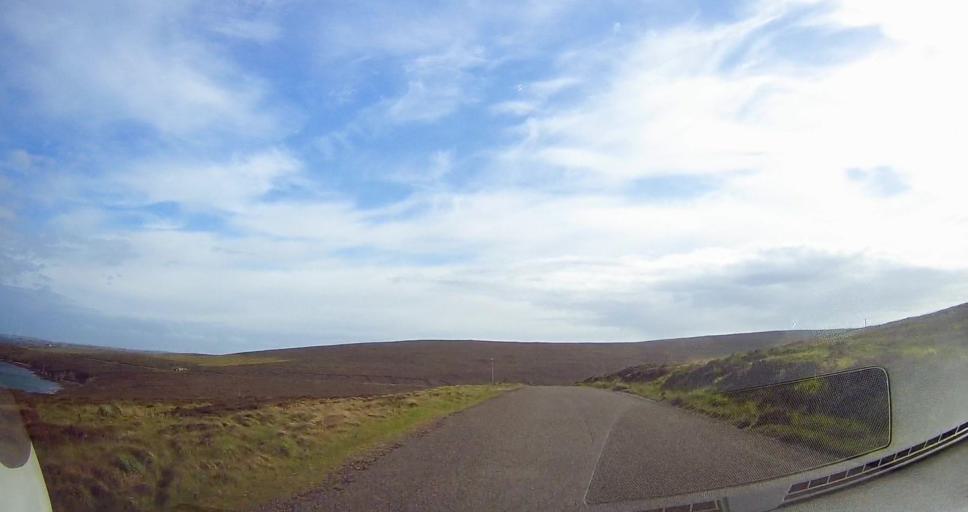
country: GB
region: Scotland
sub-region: Orkney Islands
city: Stromness
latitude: 58.8654
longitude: -3.2202
